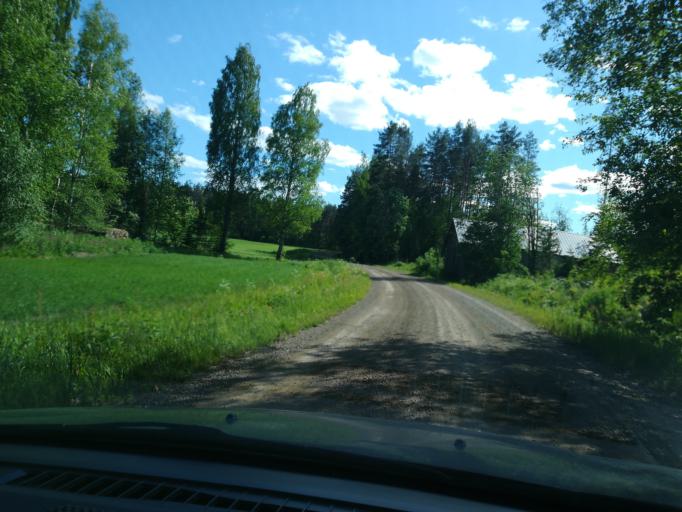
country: FI
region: Southern Savonia
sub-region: Mikkeli
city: Puumala
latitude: 61.6584
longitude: 28.1277
